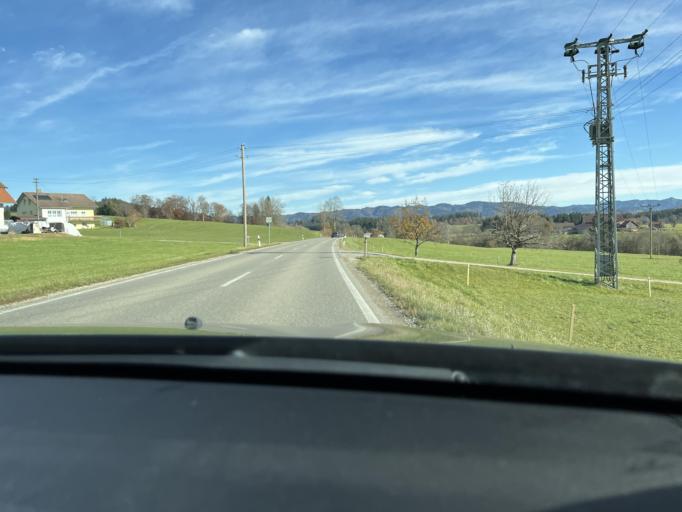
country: DE
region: Baden-Wuerttemberg
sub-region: Tuebingen Region
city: Isny im Allgau
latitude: 47.7054
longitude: 9.9875
